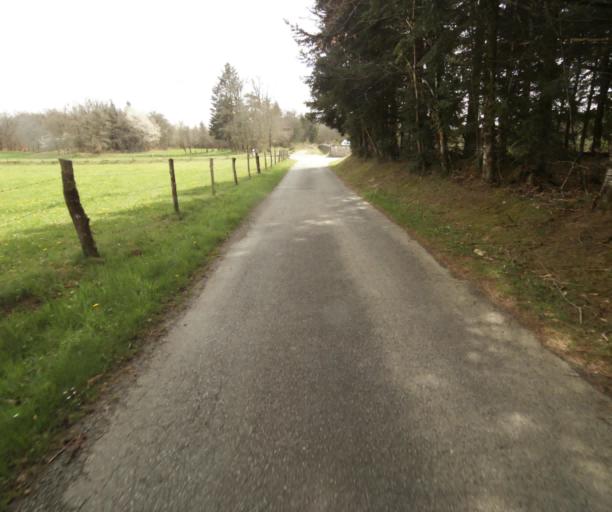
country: FR
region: Limousin
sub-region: Departement de la Correze
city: Laguenne
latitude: 45.2164
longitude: 1.9004
